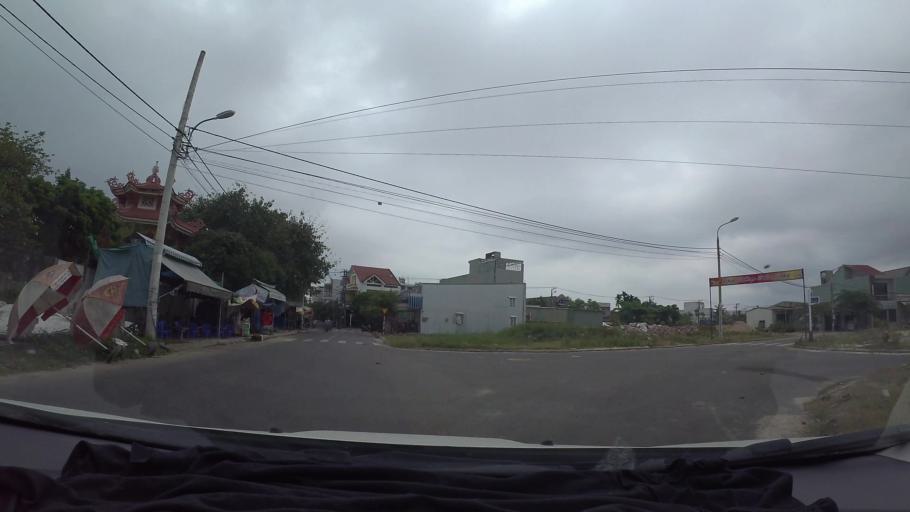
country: VN
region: Da Nang
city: Lien Chieu
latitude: 16.0501
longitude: 108.1697
